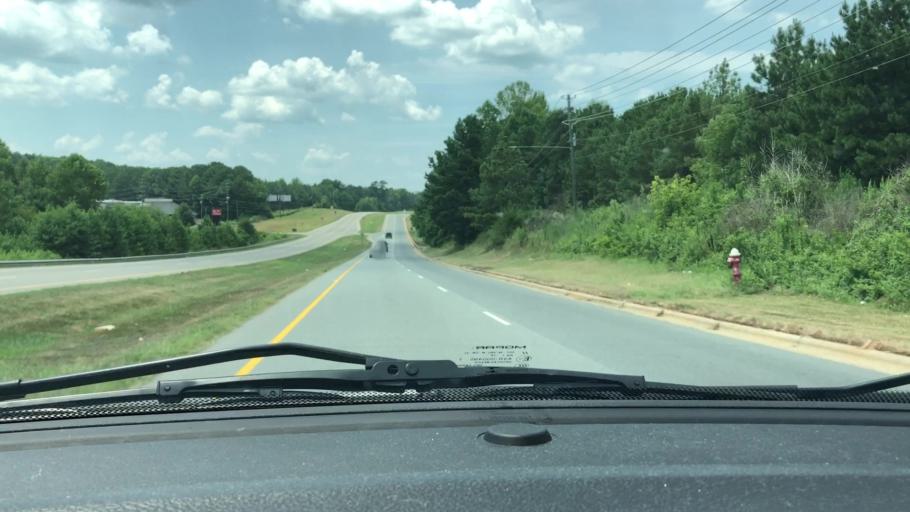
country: US
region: North Carolina
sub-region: Lee County
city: Sanford
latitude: 35.4988
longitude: -79.2004
